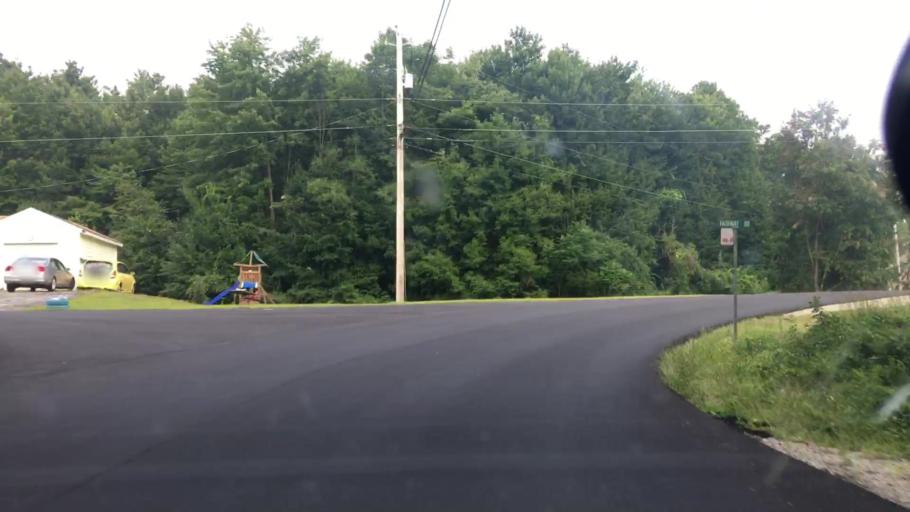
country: US
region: Maine
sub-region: Cumberland County
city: Raymond
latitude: 43.8850
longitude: -70.4625
